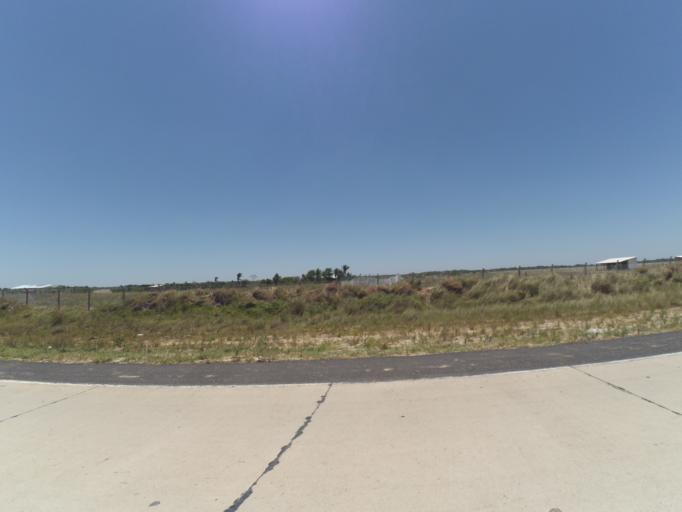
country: BO
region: Santa Cruz
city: Santa Cruz de la Sierra
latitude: -17.7961
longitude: -63.2757
